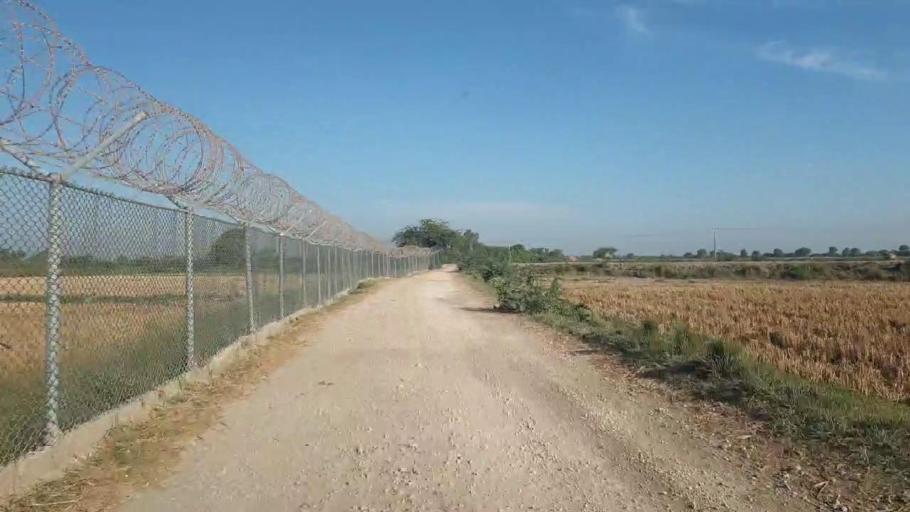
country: PK
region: Sindh
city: Talhar
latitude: 24.8517
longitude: 68.8587
